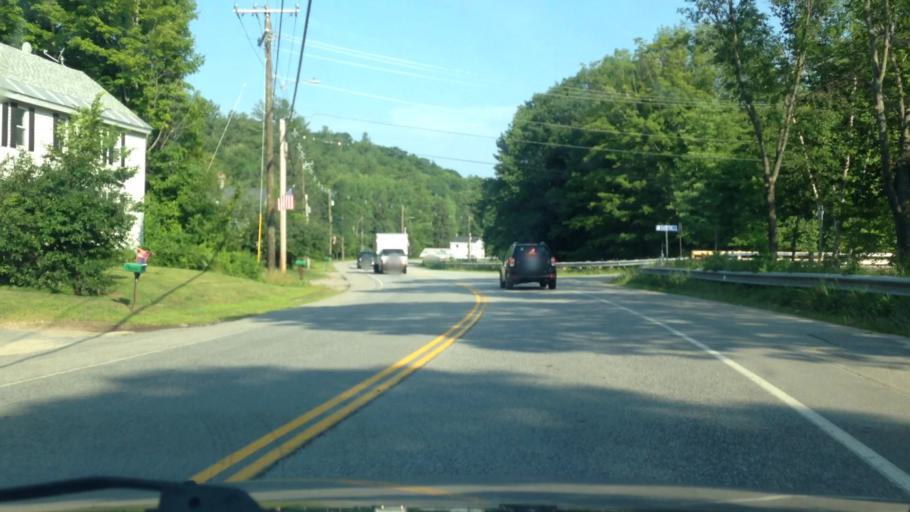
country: US
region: New Hampshire
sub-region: Cheshire County
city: Marlborough
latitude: 42.9097
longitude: -72.2186
